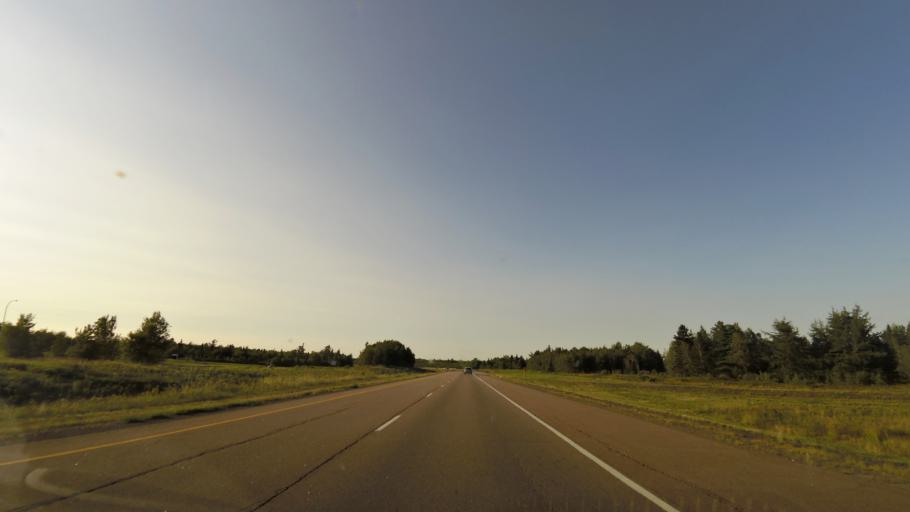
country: CA
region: New Brunswick
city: Dieppe
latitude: 46.1032
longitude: -64.6072
